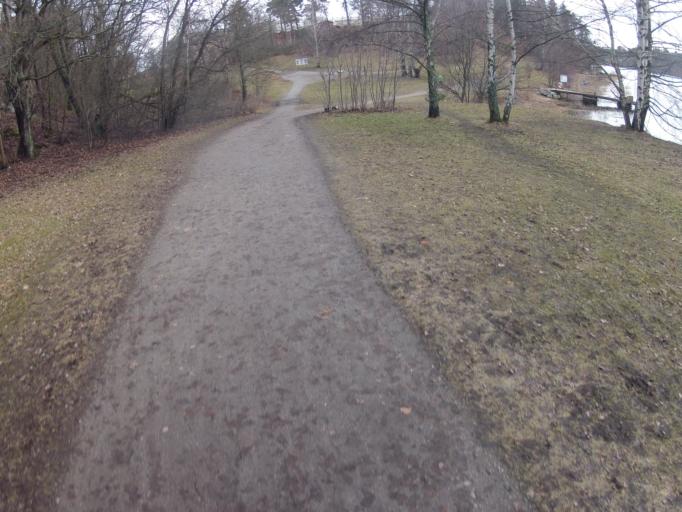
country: SE
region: Stockholm
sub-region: Norrtalje Kommun
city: Bergshamra
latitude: 59.3682
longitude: 18.0347
